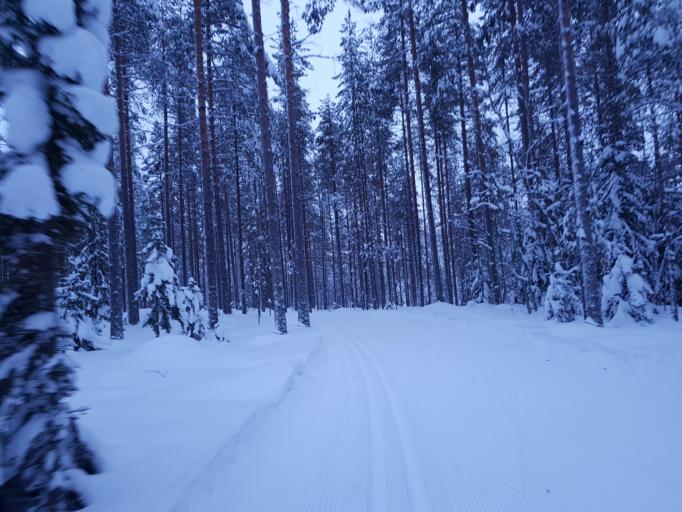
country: FI
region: Kainuu
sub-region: Kehys-Kainuu
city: Kuhmo
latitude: 64.0845
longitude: 29.5204
